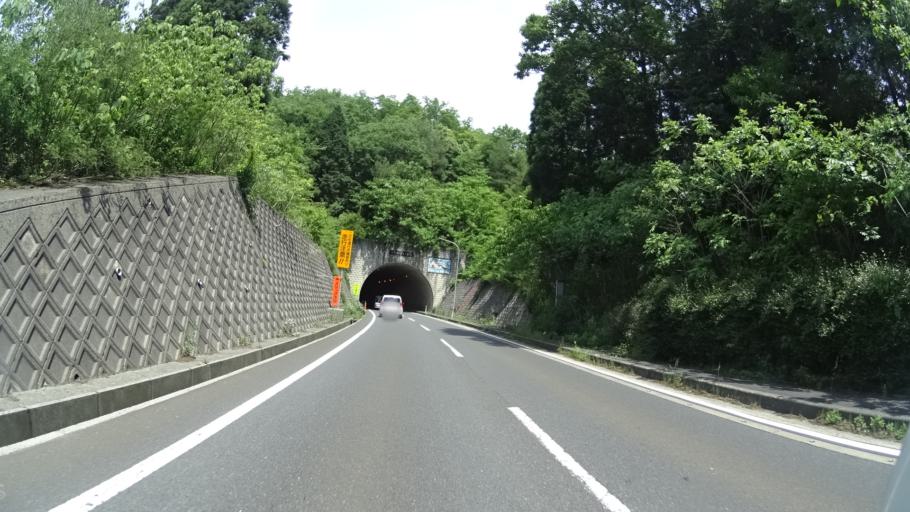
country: JP
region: Kyoto
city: Miyazu
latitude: 35.5816
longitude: 135.1175
